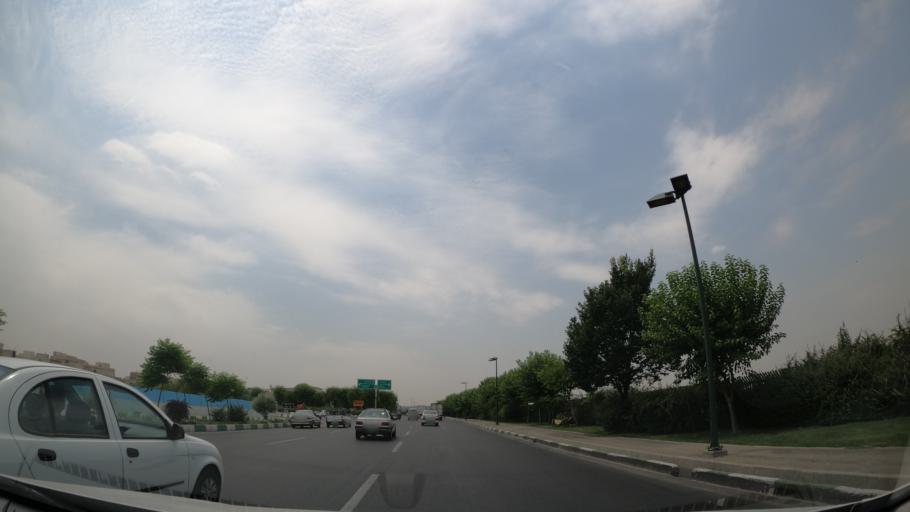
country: IR
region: Tehran
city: Tehran
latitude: 35.6804
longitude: 51.3392
